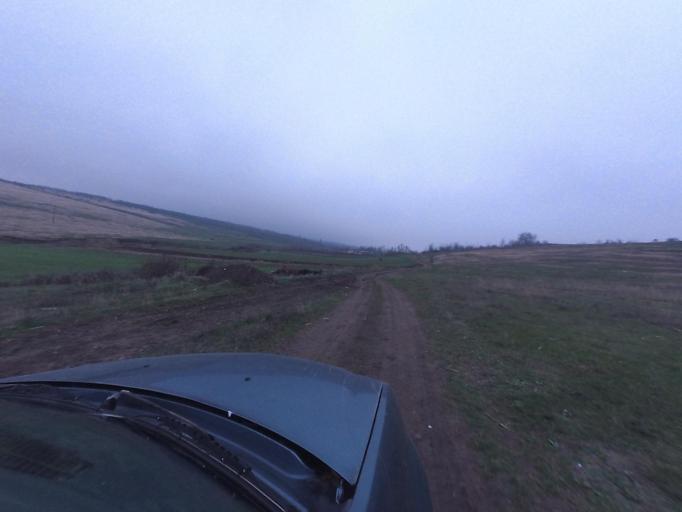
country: RO
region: Galati
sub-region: Comuna Balabanesti
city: Balabanesti
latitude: 46.1327
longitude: 27.7499
